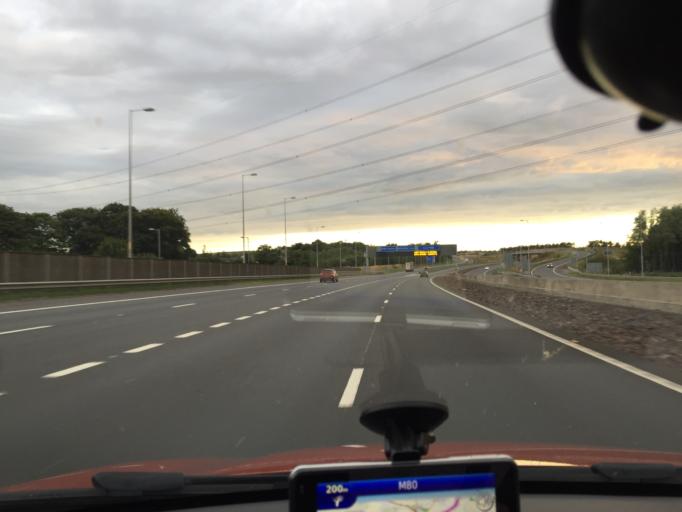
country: GB
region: Scotland
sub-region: North Lanarkshire
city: Glenboig
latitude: 55.9252
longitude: -4.0467
